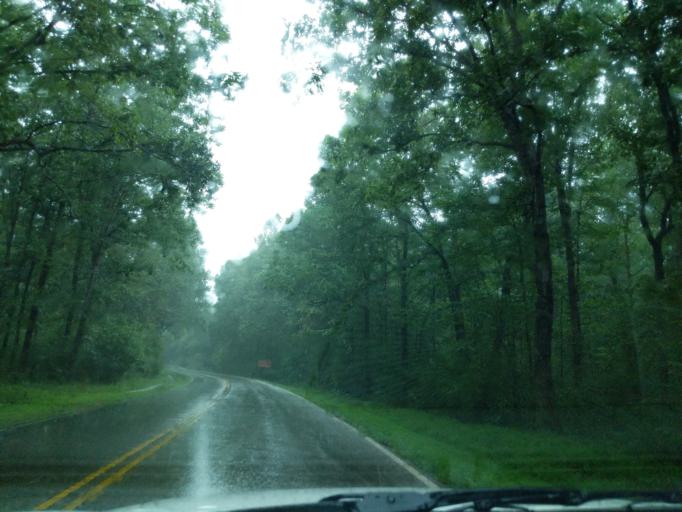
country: US
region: Kentucky
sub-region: Barren County
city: Cave City
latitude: 37.1791
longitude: -86.0895
